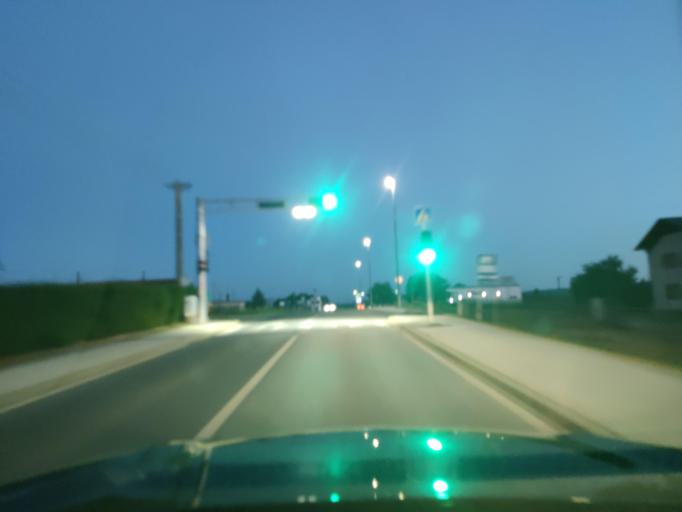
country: HR
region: Medimurska
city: Vratisinec
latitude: 46.5050
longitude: 16.4316
